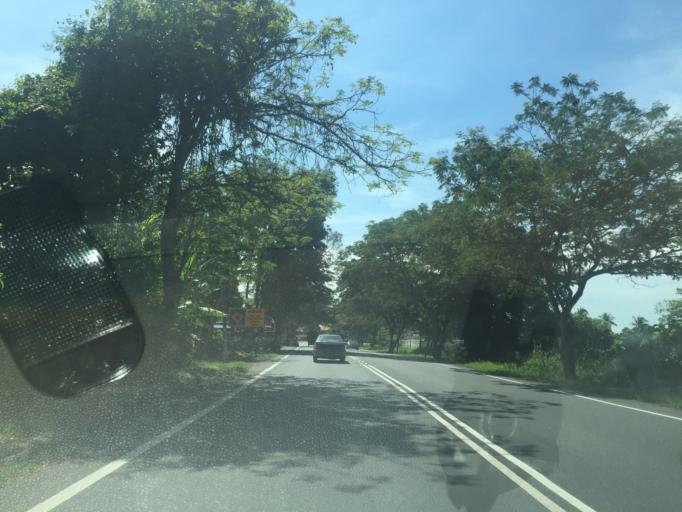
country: MY
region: Penang
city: Tasek Glugor
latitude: 5.4716
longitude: 100.4571
